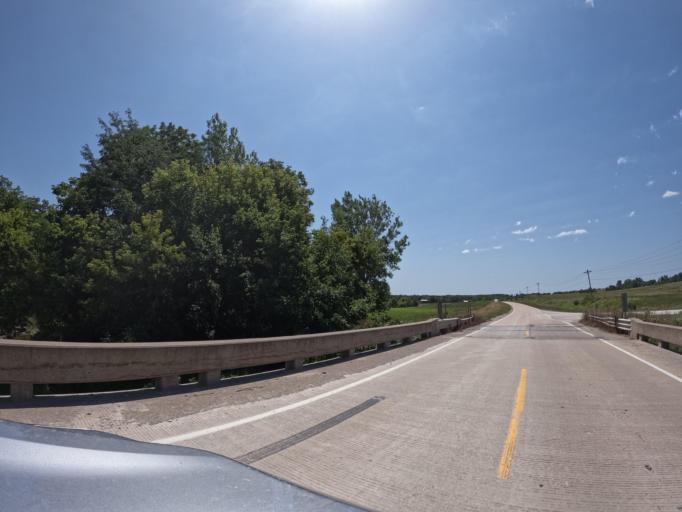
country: US
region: Iowa
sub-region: Henry County
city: Mount Pleasant
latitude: 40.9293
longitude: -91.5548
